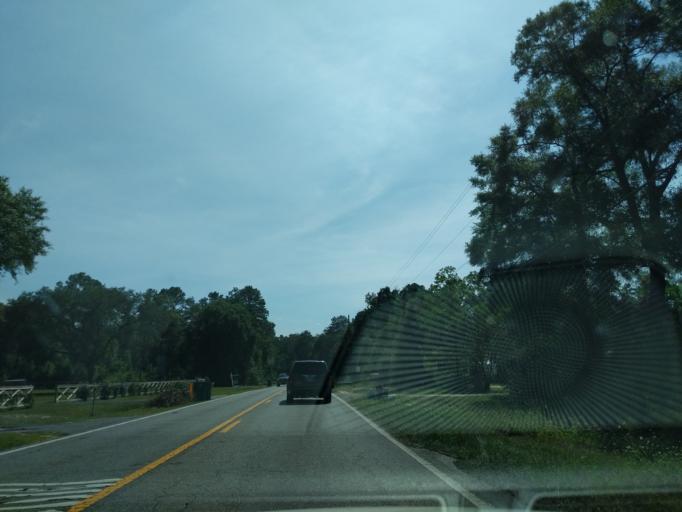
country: US
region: Florida
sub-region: Okaloosa County
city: Crestview
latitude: 30.7507
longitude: -86.6201
